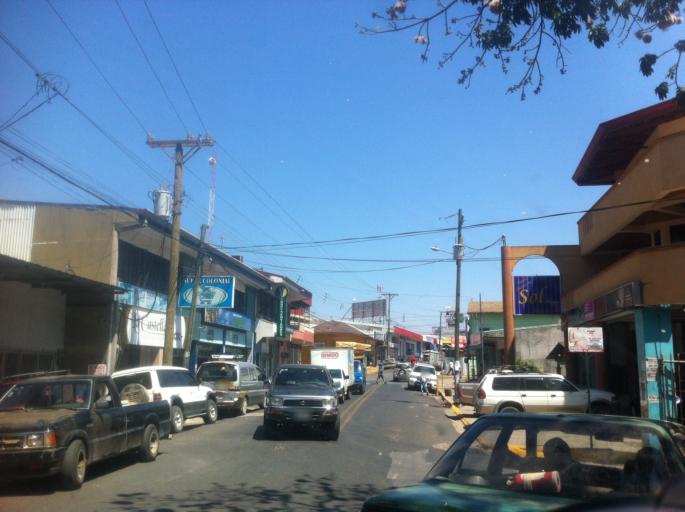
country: CR
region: Guanacaste
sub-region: Canton de Nicoya
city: Nicoya
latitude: 10.1347
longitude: -85.4461
